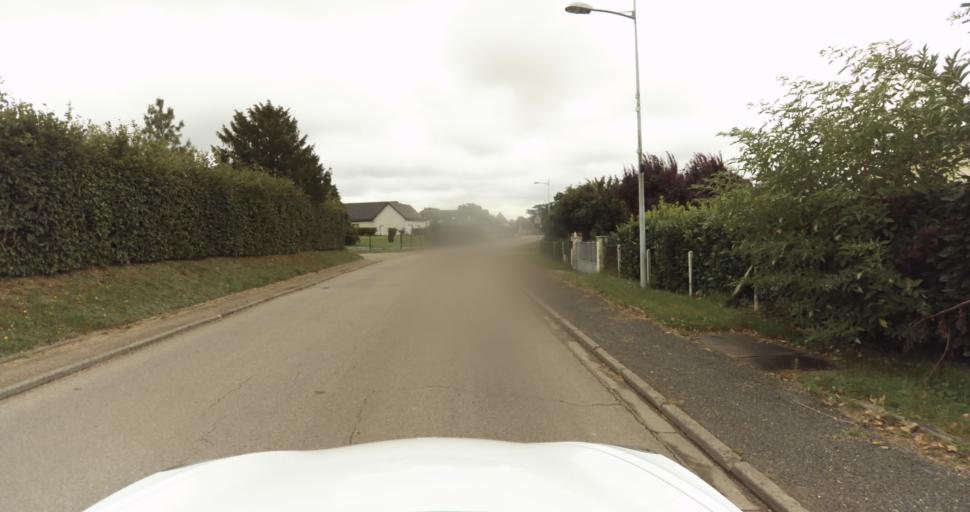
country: FR
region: Haute-Normandie
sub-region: Departement de l'Eure
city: Aviron
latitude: 49.0554
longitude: 1.0867
